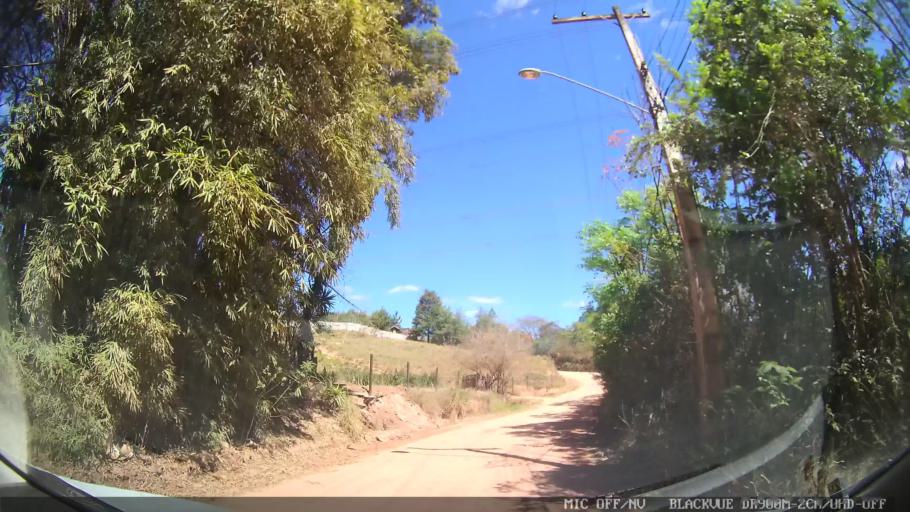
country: BR
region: Sao Paulo
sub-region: Jarinu
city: Jarinu
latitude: -23.1579
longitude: -46.7149
